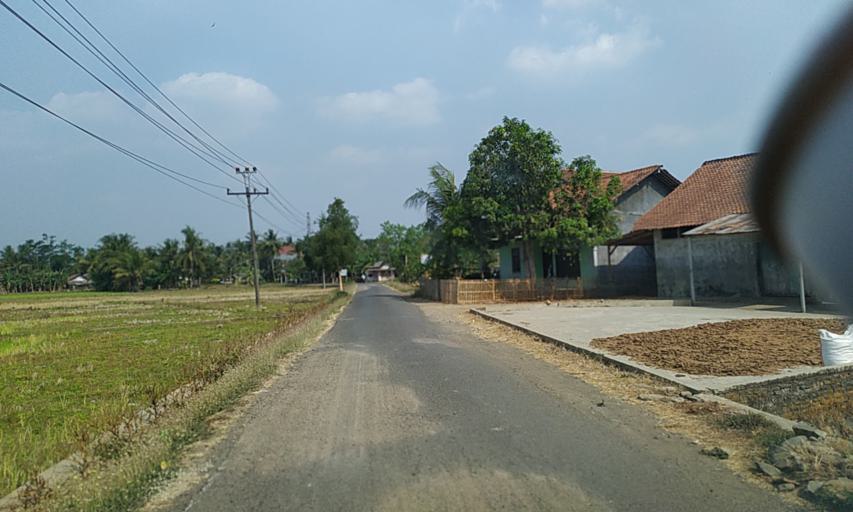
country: ID
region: Central Java
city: Kutasari
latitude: -7.3105
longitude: 108.7809
